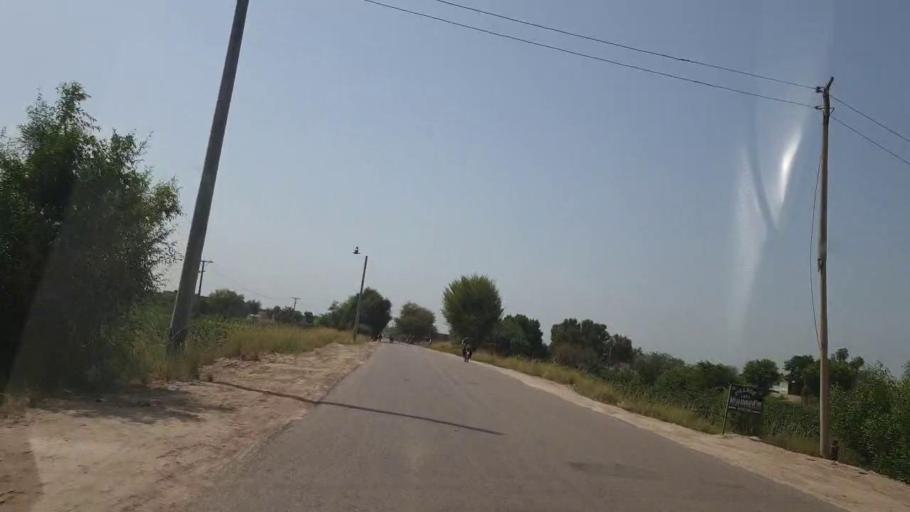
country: PK
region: Sindh
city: Setharja Old
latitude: 27.1277
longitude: 68.5375
